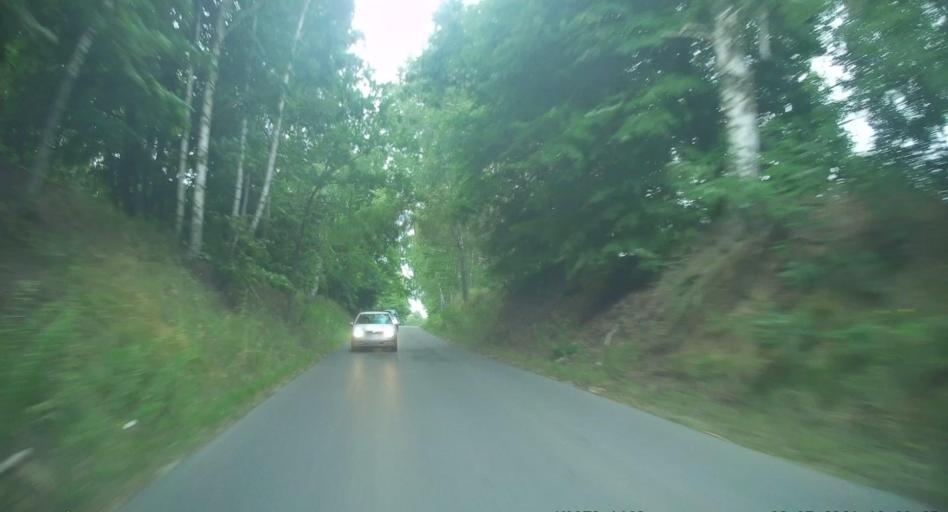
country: PL
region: Lodz Voivodeship
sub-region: Powiat rawski
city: Rawa Mazowiecka
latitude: 51.7436
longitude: 20.2035
